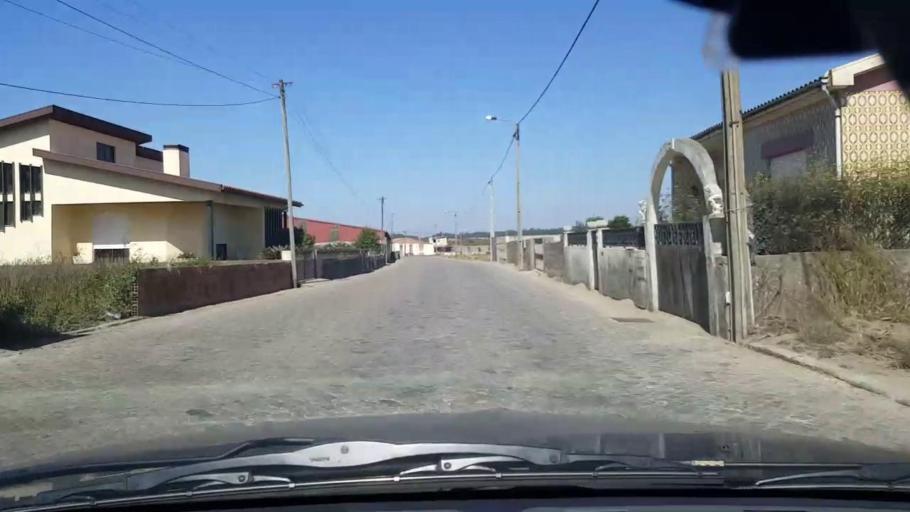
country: PT
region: Porto
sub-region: Matosinhos
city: Lavra
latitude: 41.2830
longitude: -8.7241
